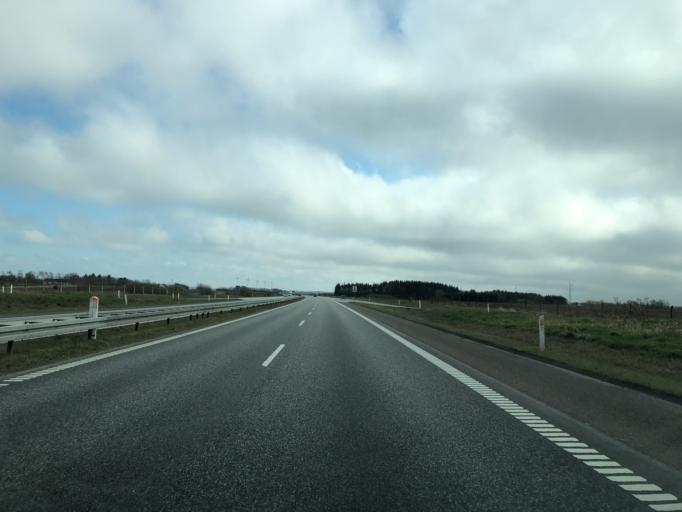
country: DK
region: North Denmark
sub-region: Hjorring Kommune
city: Hjorring
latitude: 57.4224
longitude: 10.0292
